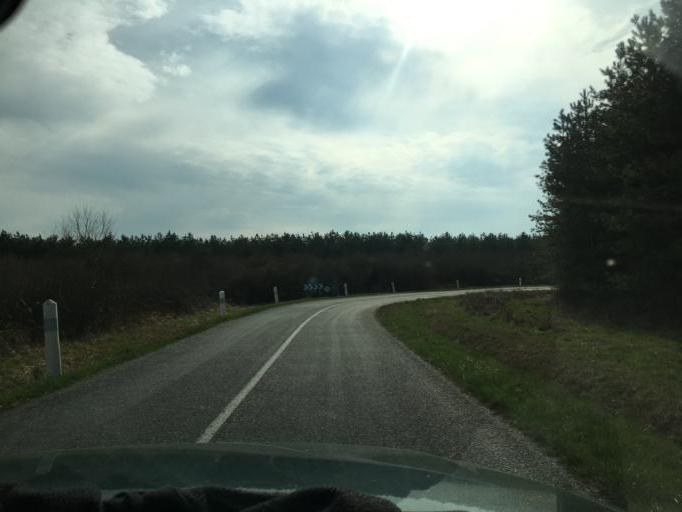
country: FR
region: Centre
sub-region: Departement du Loiret
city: La Ferte-Saint-Aubin
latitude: 47.7697
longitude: 1.9358
